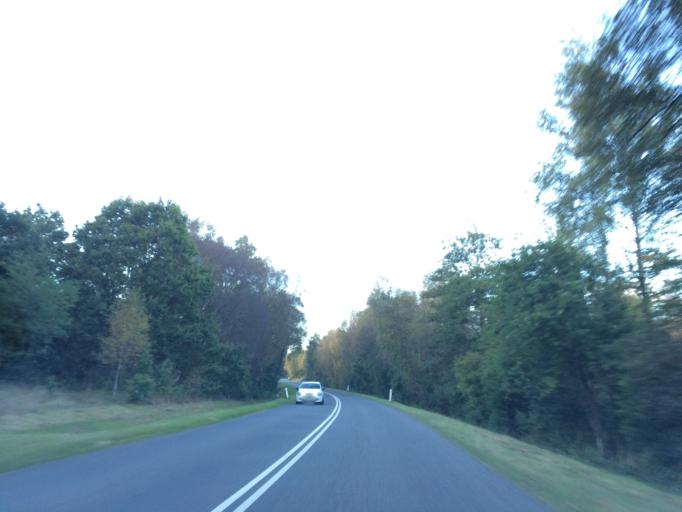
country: DK
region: Central Jutland
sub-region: Skanderborg Kommune
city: Ry
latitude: 56.1015
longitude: 9.7397
